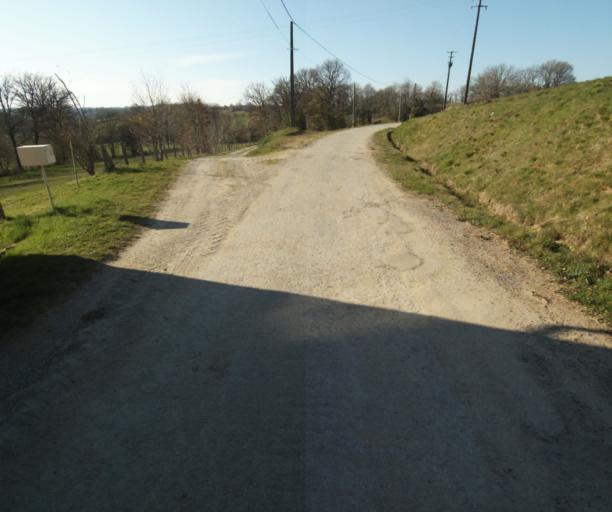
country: FR
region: Limousin
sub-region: Departement de la Correze
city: Chamboulive
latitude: 45.4978
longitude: 1.7254
